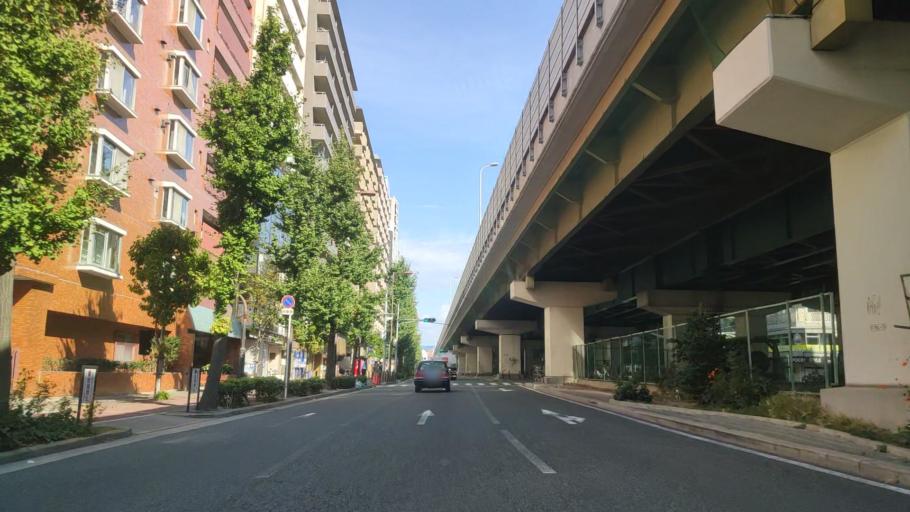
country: JP
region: Osaka
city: Suita
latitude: 34.7438
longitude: 135.4979
